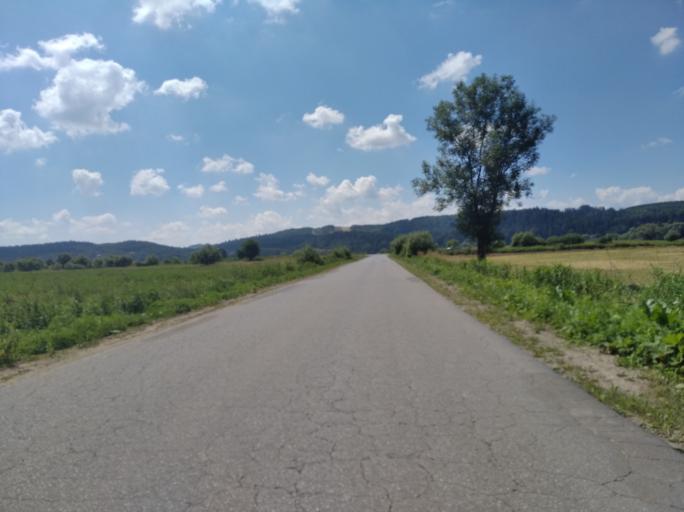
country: PL
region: Subcarpathian Voivodeship
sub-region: Powiat brzozowski
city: Dydnia
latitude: 49.7044
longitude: 22.2092
